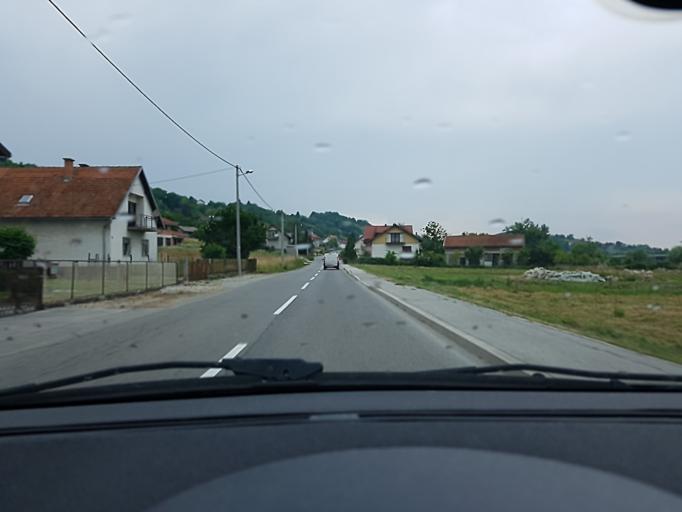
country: HR
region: Zagrebacka
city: Pojatno
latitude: 45.9143
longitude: 15.8082
